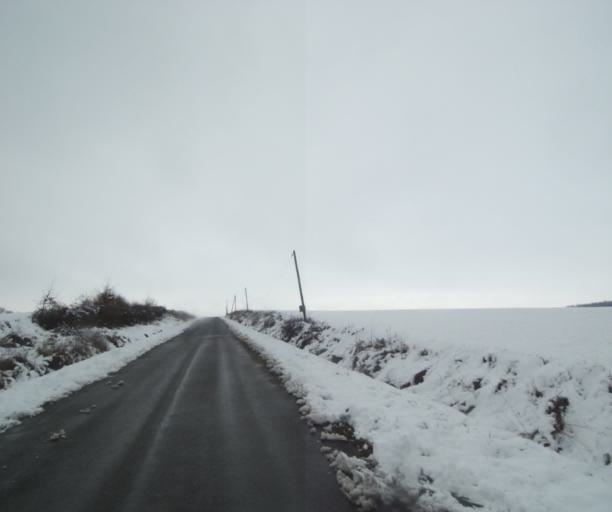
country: FR
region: Champagne-Ardenne
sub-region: Departement de la Haute-Marne
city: Montier-en-Der
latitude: 48.4628
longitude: 4.8241
